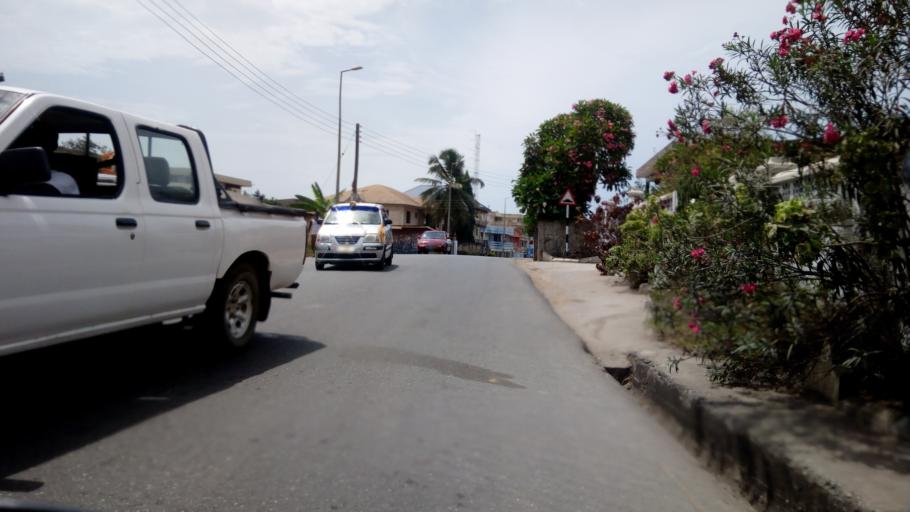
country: GH
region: Central
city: Cape Coast
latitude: 5.1320
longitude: -1.2768
